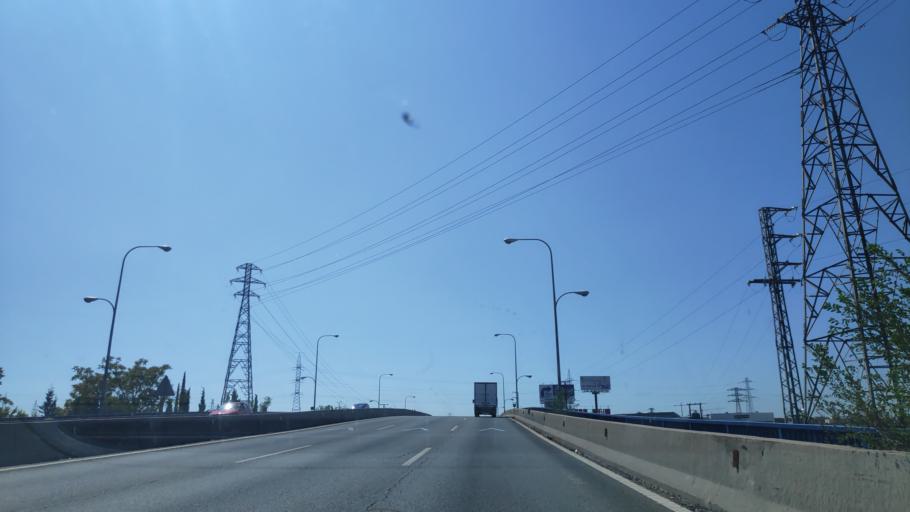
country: ES
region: Madrid
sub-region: Provincia de Madrid
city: Villaverde
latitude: 40.3389
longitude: -3.7244
